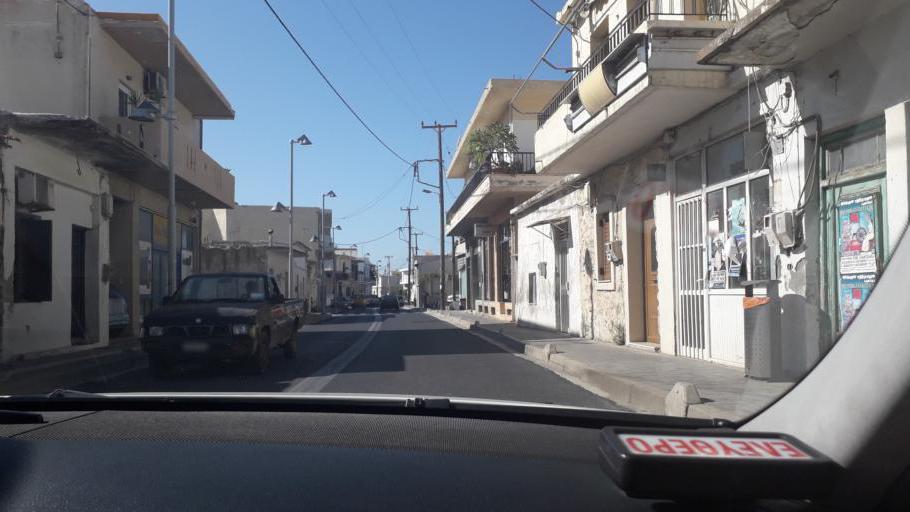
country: GR
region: Crete
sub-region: Nomos Rethymnis
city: Rethymno
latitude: 35.3662
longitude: 24.5067
